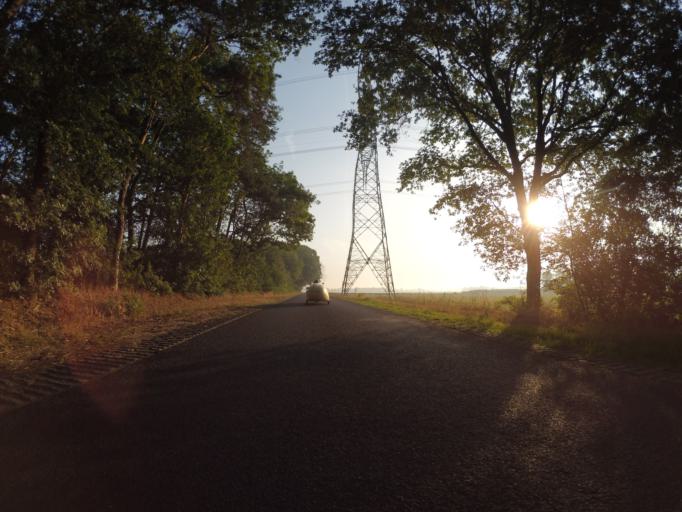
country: NL
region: Overijssel
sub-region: Gemeente Wierden
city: Wierden
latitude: 52.3962
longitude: 6.5315
